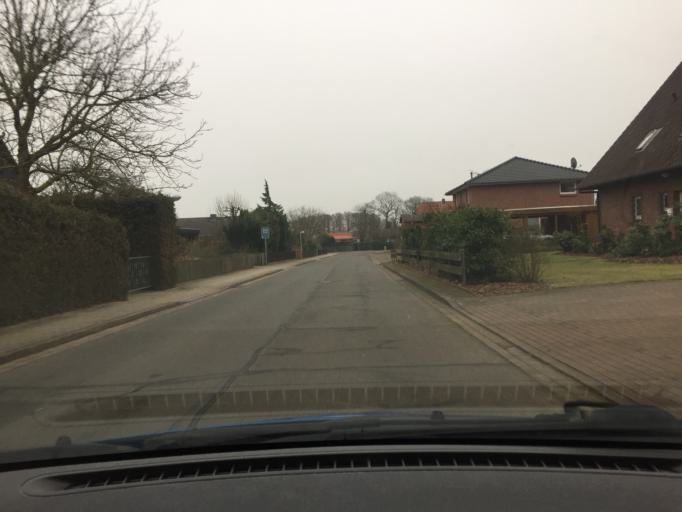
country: DE
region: Lower Saxony
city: Kirchgellersen
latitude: 53.2322
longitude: 10.2922
